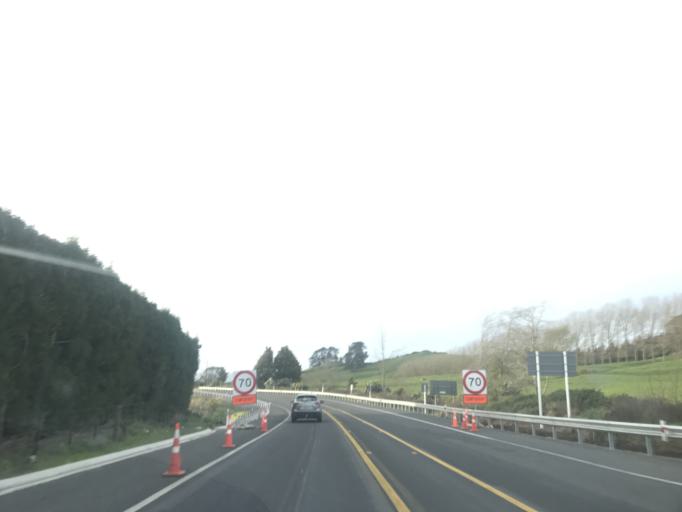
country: NZ
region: Bay of Plenty
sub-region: Western Bay of Plenty District
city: Waihi Beach
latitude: -37.4468
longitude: 175.8783
